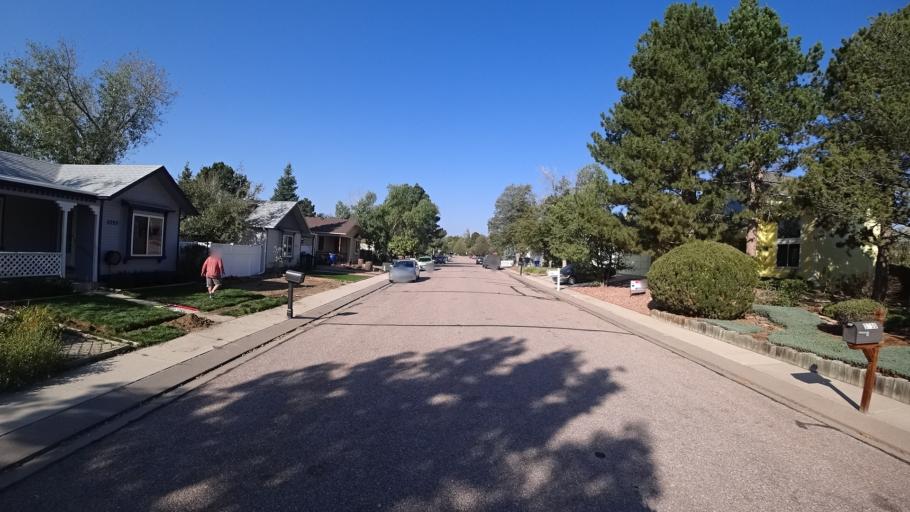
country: US
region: Colorado
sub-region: El Paso County
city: Cimarron Hills
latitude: 38.8833
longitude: -104.7214
